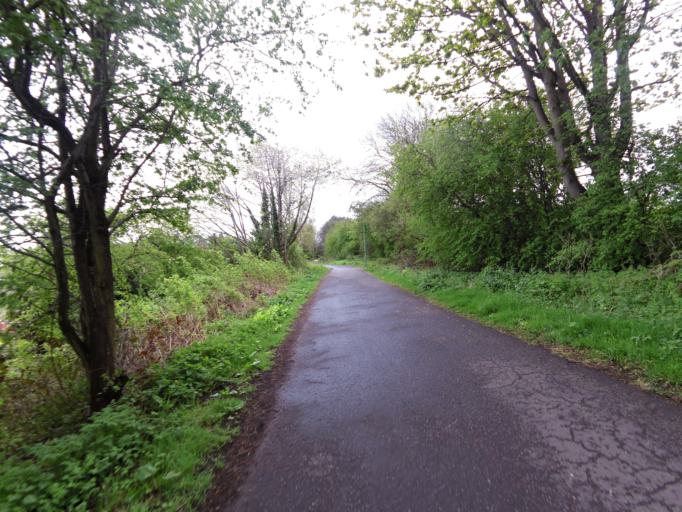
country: GB
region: Scotland
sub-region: Edinburgh
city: Edinburgh
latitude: 55.9531
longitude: -3.2401
